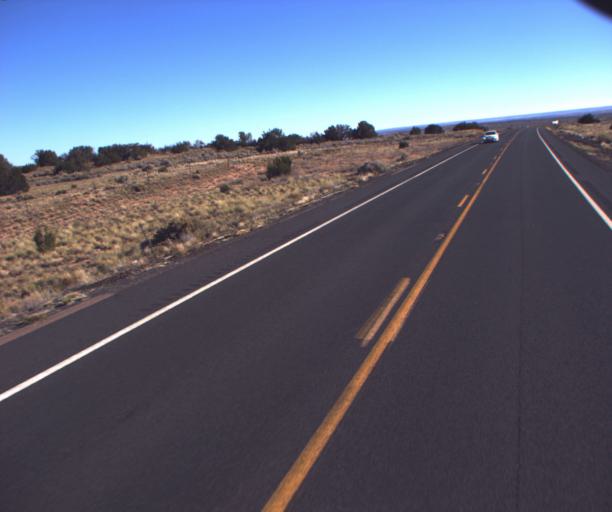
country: US
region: Arizona
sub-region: Apache County
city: Houck
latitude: 35.3213
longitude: -109.4327
